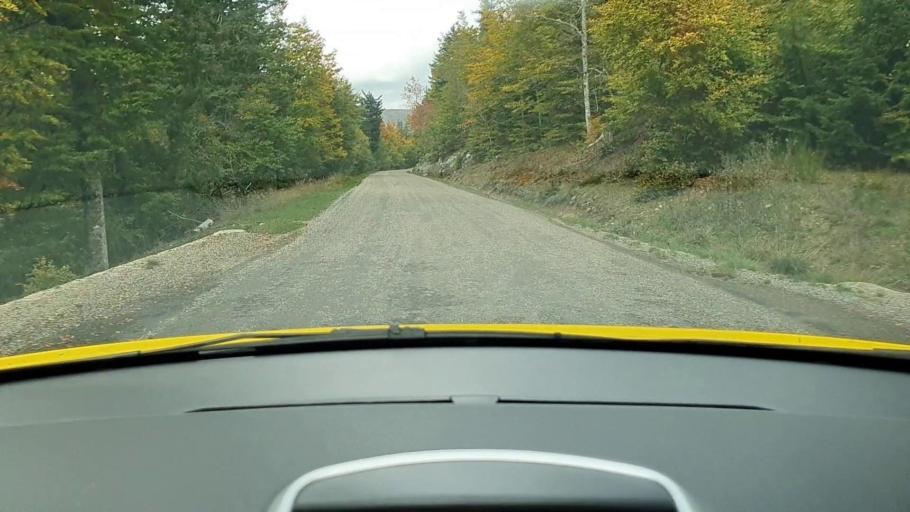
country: FR
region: Languedoc-Roussillon
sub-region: Departement du Gard
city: Le Vigan
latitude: 44.0553
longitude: 3.5473
